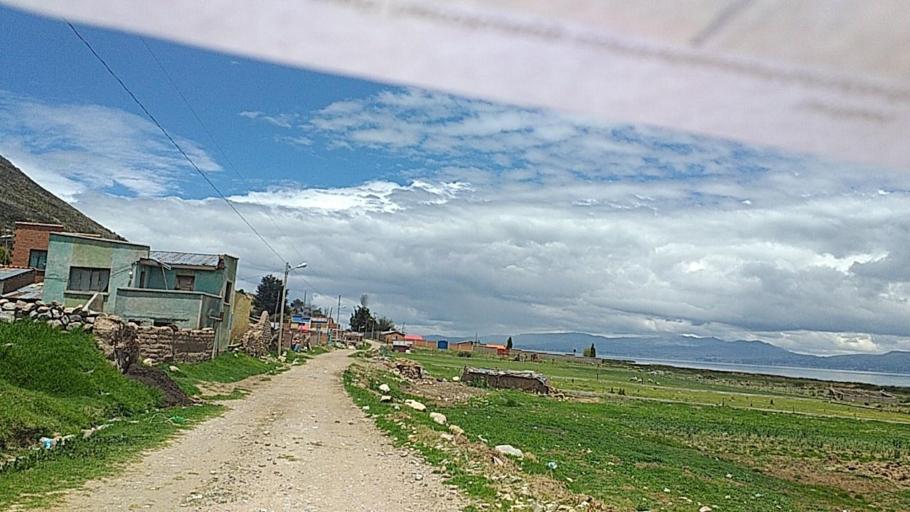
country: BO
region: La Paz
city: Huatajata
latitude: -16.3142
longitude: -68.6747
